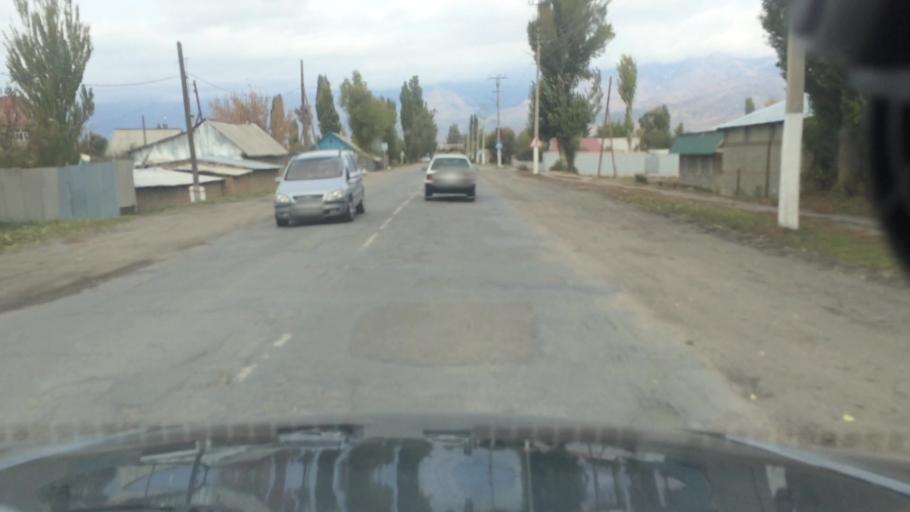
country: KG
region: Ysyk-Koel
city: Tyup
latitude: 42.7233
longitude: 78.3662
